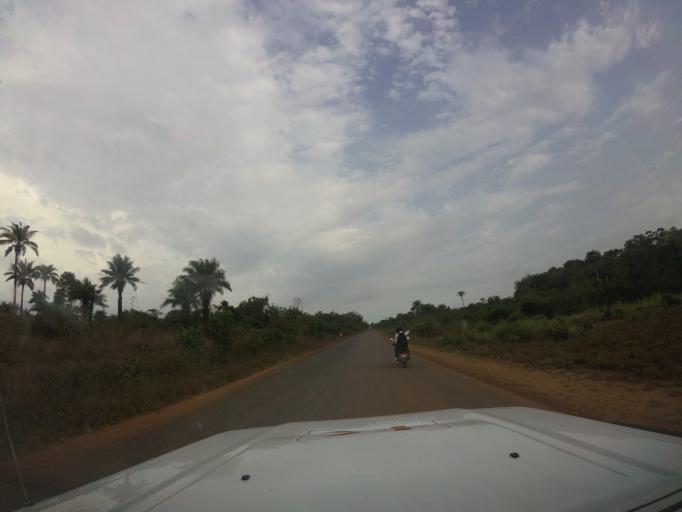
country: LR
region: Bomi
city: Tubmanburg
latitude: 6.7301
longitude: -10.9906
